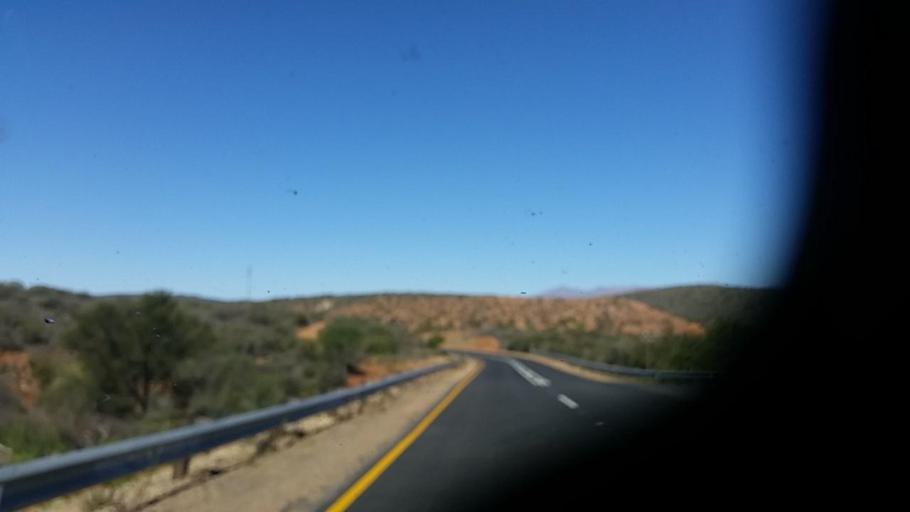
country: ZA
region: Western Cape
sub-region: Eden District Municipality
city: Oudtshoorn
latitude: -33.4771
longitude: 22.6412
